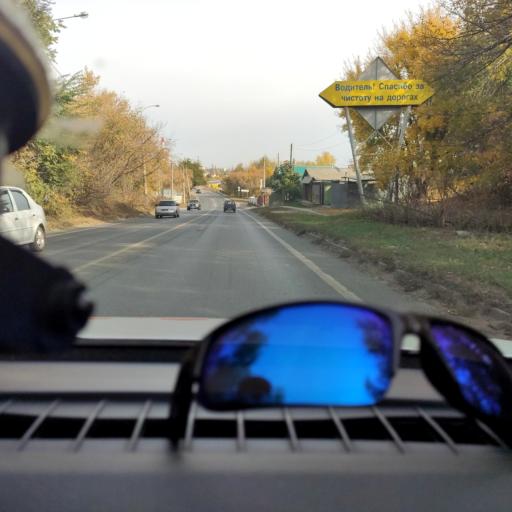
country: RU
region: Samara
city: Novokuybyshevsk
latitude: 53.0901
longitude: 50.0656
